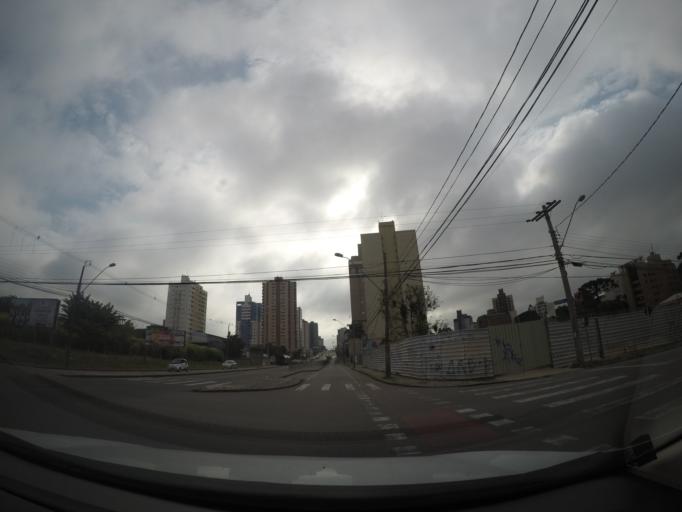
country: BR
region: Parana
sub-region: Curitiba
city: Curitiba
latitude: -25.4042
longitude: -49.2504
